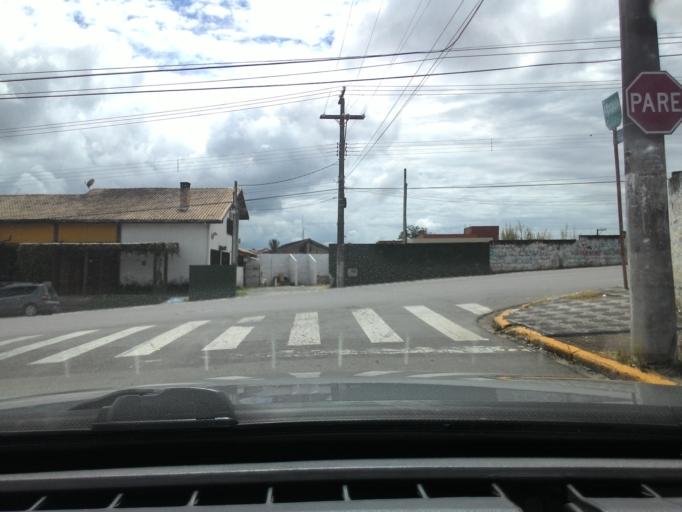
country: BR
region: Sao Paulo
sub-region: Registro
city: Registro
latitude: -24.4996
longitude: -47.8413
